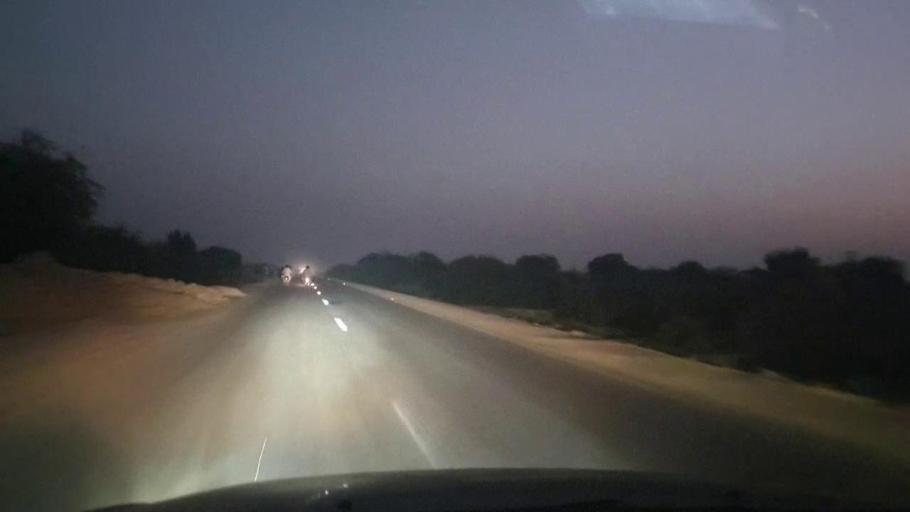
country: PK
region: Sindh
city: Chambar
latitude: 25.3516
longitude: 68.7898
